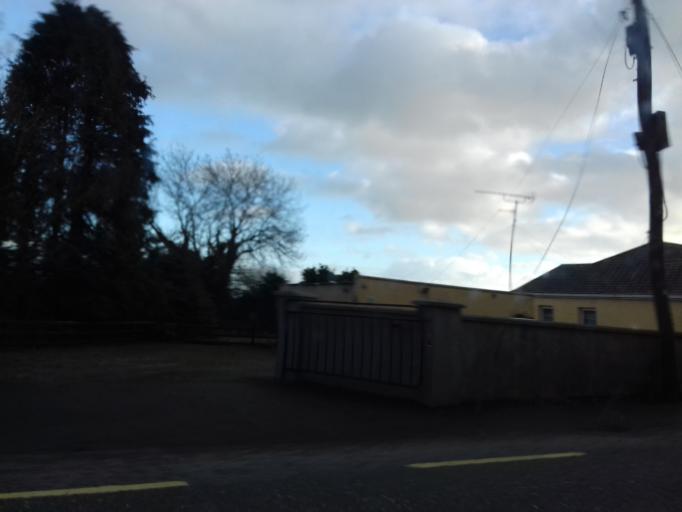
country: IE
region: Leinster
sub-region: An Mhi
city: Slane
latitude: 53.7553
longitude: -6.4969
